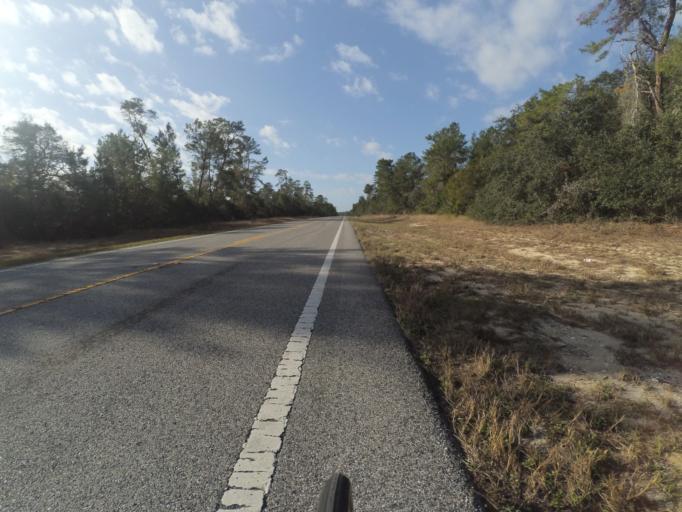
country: US
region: Florida
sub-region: Lake County
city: Astor
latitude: 29.1353
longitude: -81.6021
